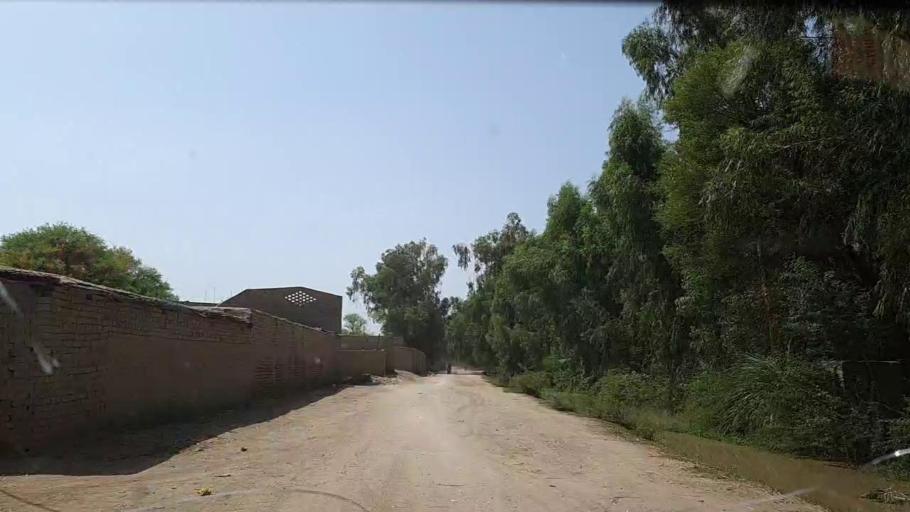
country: PK
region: Sindh
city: Ghotki
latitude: 28.0908
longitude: 69.3324
